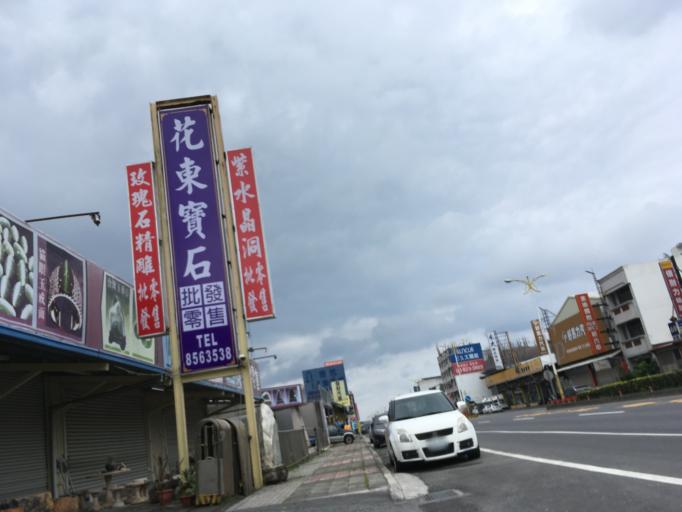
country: TW
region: Taiwan
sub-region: Hualien
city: Hualian
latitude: 23.9986
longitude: 121.5965
